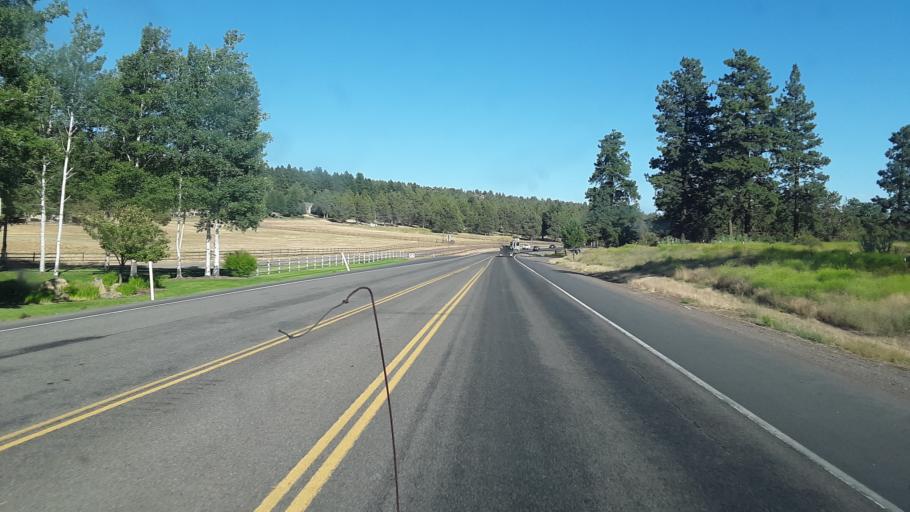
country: US
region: Oregon
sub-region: Klamath County
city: Klamath Falls
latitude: 42.2718
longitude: -121.8838
